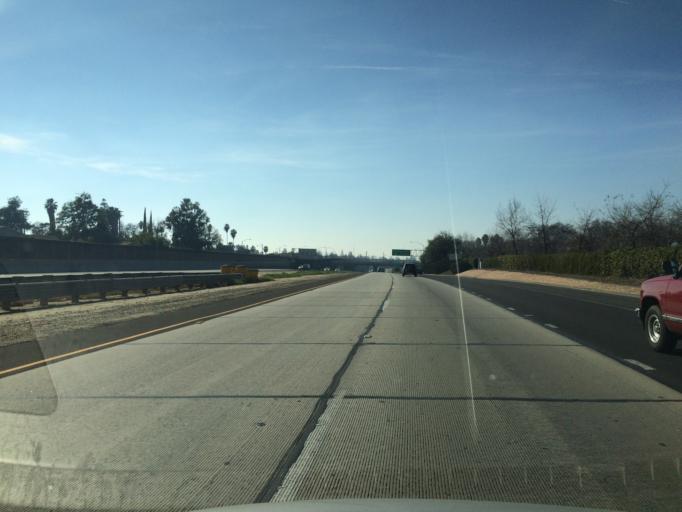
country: US
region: California
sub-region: Tulare County
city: Visalia
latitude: 36.3276
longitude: -119.3211
